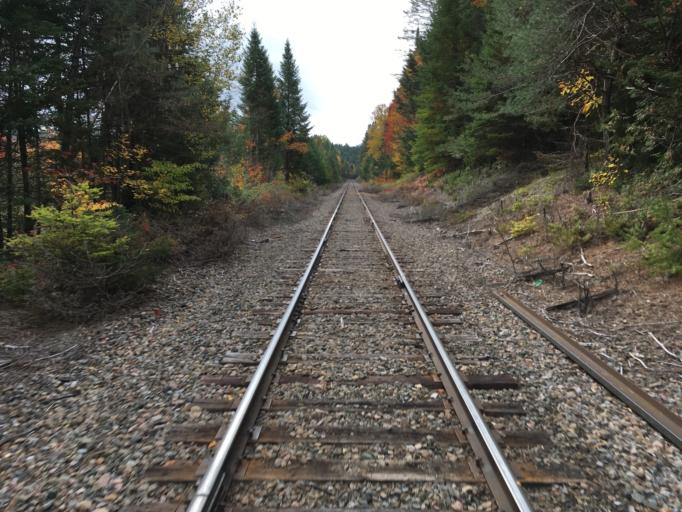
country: US
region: Vermont
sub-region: Caledonia County
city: Lyndonville
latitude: 44.6210
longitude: -71.9666
